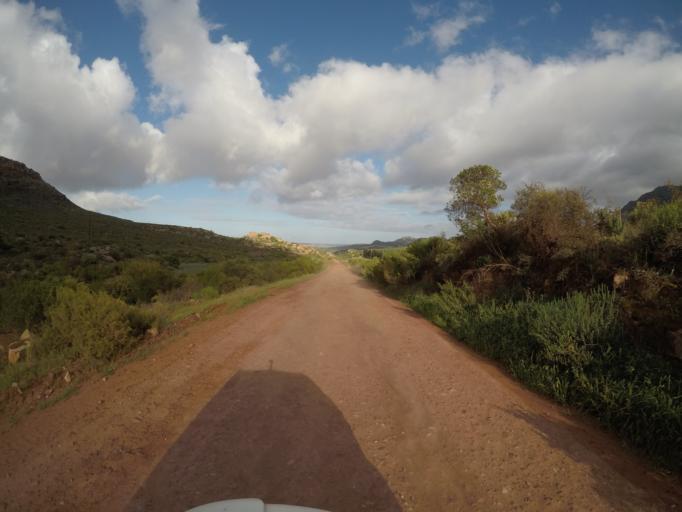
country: ZA
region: Western Cape
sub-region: West Coast District Municipality
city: Clanwilliam
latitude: -32.3400
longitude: 18.7677
